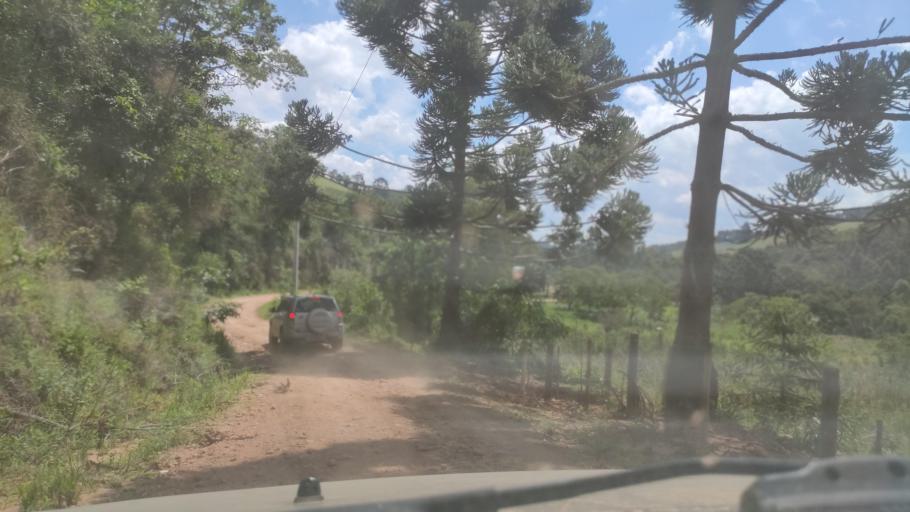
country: BR
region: Minas Gerais
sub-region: Cambui
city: Cambui
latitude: -22.6914
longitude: -45.9777
